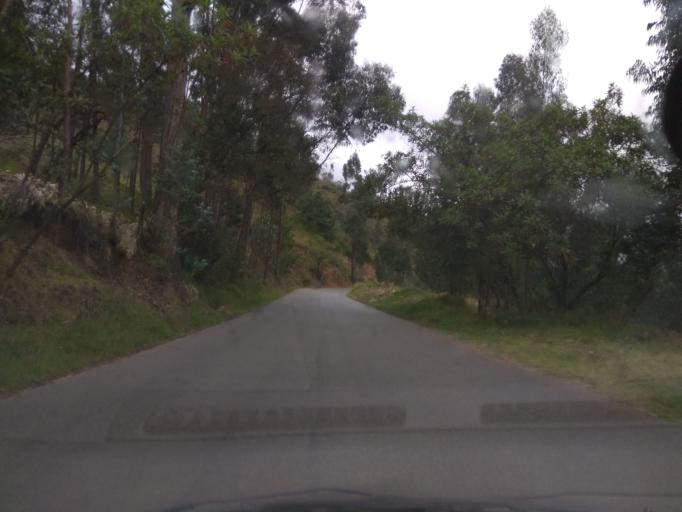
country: CO
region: Boyaca
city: Topaga
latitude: 5.7654
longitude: -72.8517
